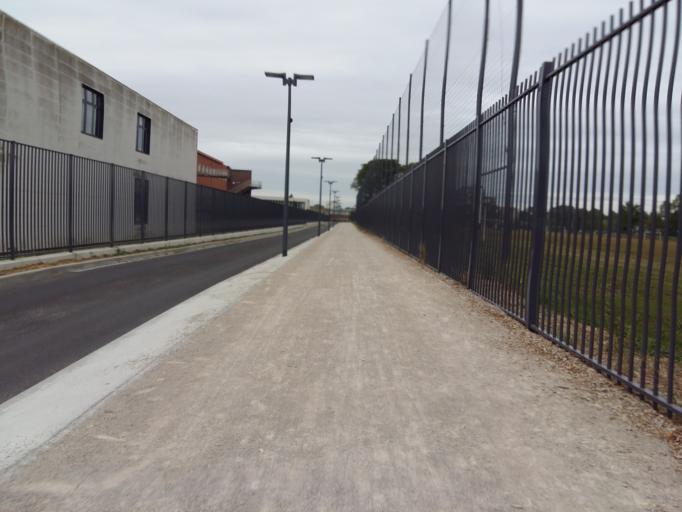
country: FR
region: Picardie
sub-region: Departement de la Somme
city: Amiens
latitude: 49.8762
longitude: 2.3005
